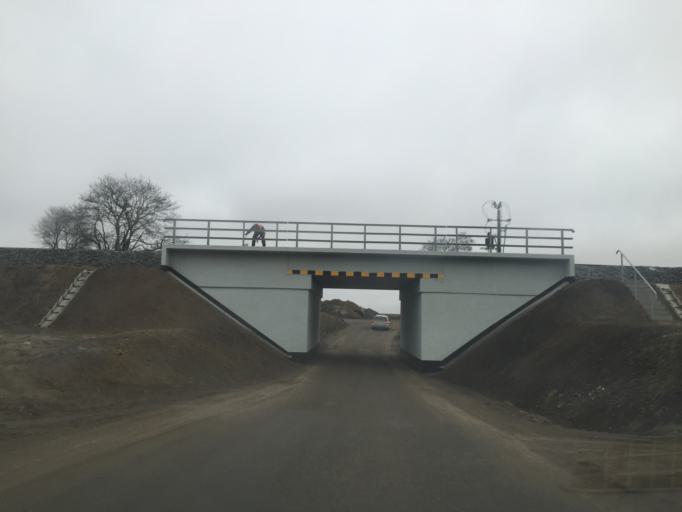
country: PL
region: Pomeranian Voivodeship
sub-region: Powiat kartuski
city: Banino
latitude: 54.4050
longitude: 18.4394
